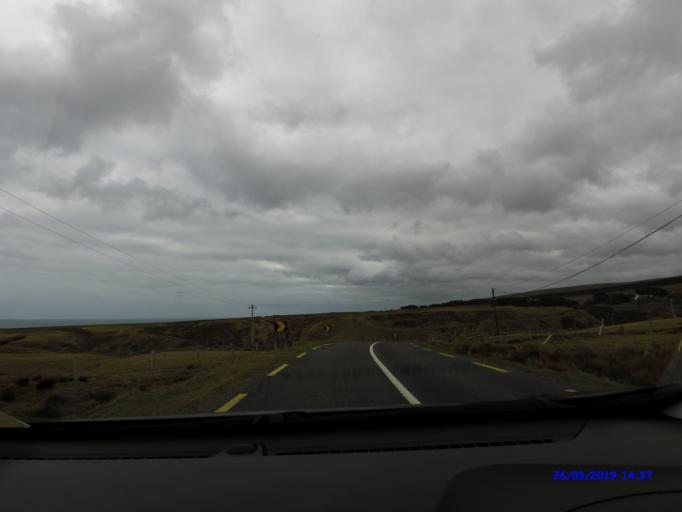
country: IE
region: Connaught
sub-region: Maigh Eo
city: Crossmolina
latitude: 54.3101
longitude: -9.5064
